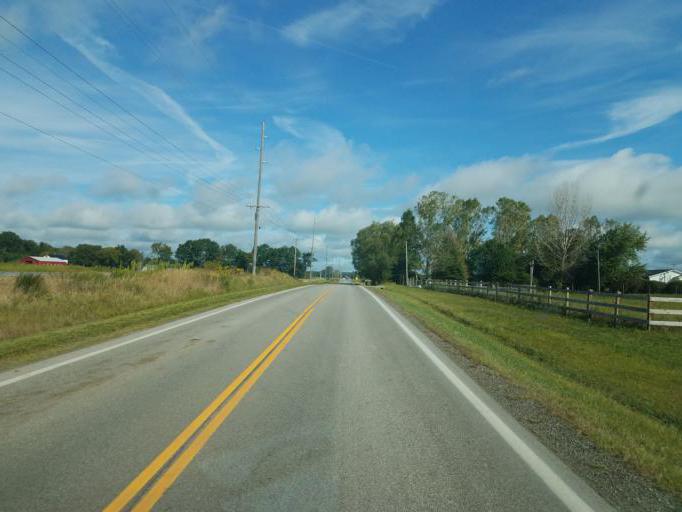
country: US
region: Ohio
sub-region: Wayne County
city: West Salem
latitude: 41.0088
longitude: -82.1172
